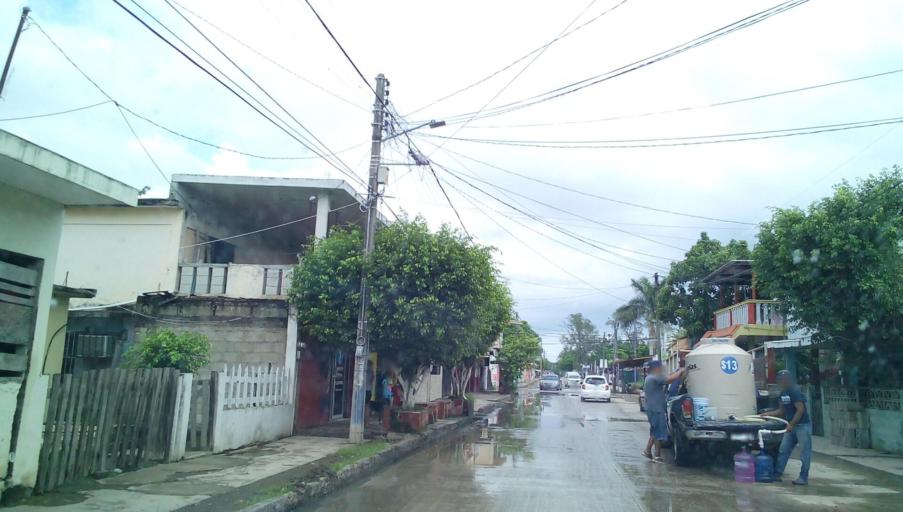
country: MX
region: Veracruz
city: Anahuac
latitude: 22.2035
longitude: -97.8418
